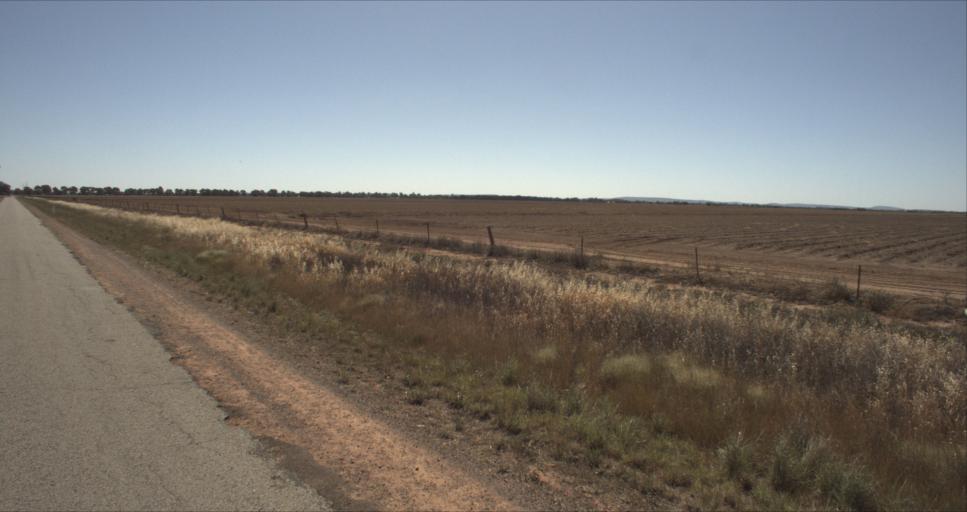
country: AU
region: New South Wales
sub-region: Leeton
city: Leeton
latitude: -34.5624
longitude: 146.3124
